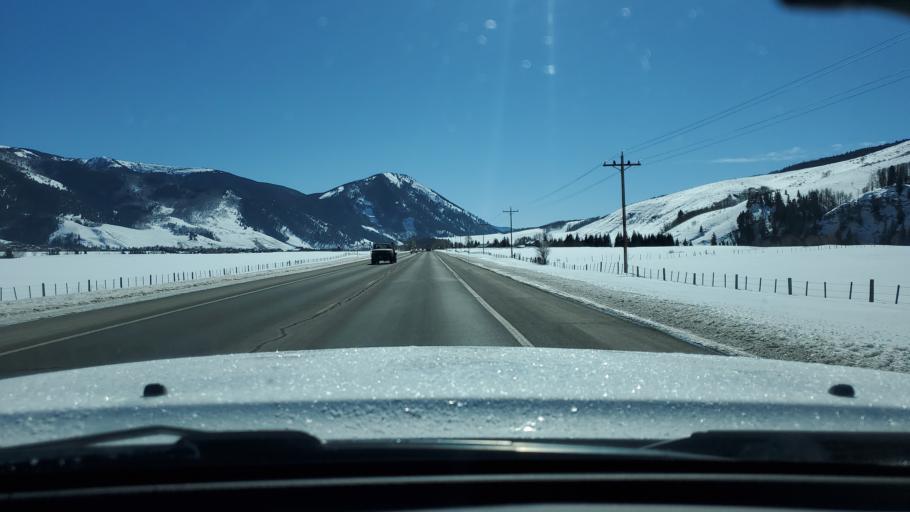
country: US
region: Colorado
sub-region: Gunnison County
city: Crested Butte
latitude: 38.8210
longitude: -106.9131
